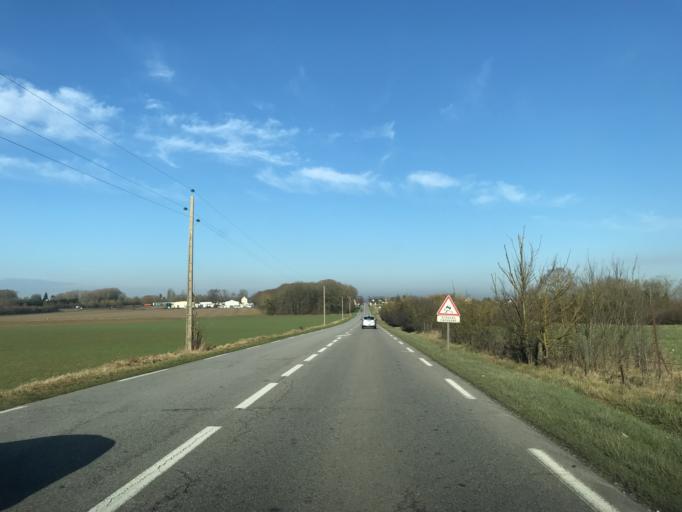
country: FR
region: Haute-Normandie
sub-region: Departement de l'Eure
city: Ande
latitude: 49.2004
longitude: 1.2318
